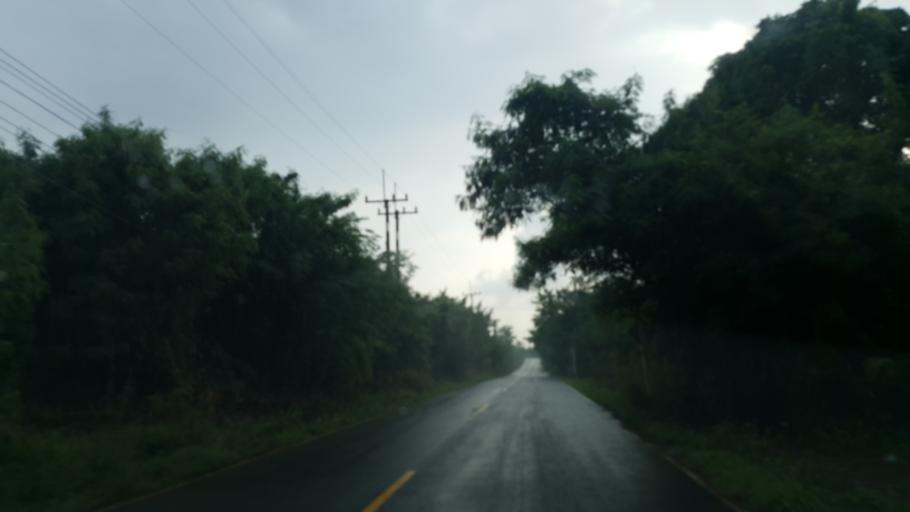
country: TH
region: Chon Buri
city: Sattahip
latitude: 12.7096
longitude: 100.9095
